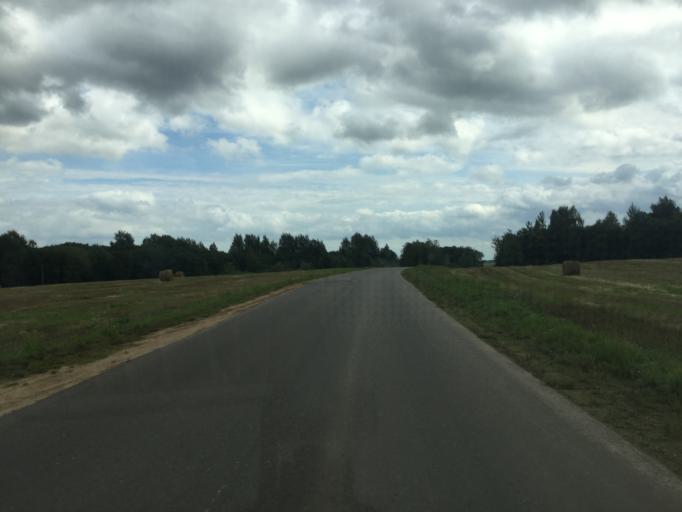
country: BY
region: Vitebsk
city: Vitebsk
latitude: 55.1273
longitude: 30.3202
